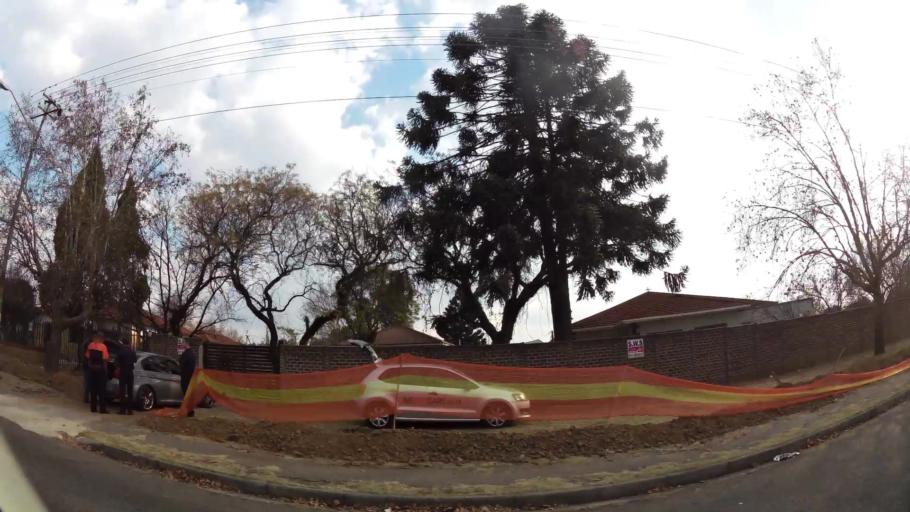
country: ZA
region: Gauteng
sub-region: Ekurhuleni Metropolitan Municipality
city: Germiston
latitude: -26.2405
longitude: 28.1699
